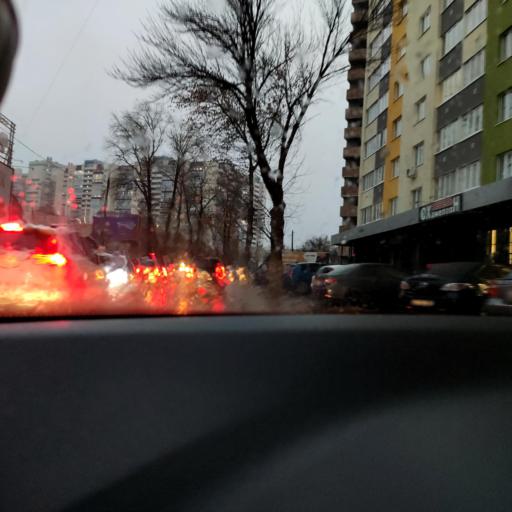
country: RU
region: Samara
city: Samara
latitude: 53.2065
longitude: 50.1772
